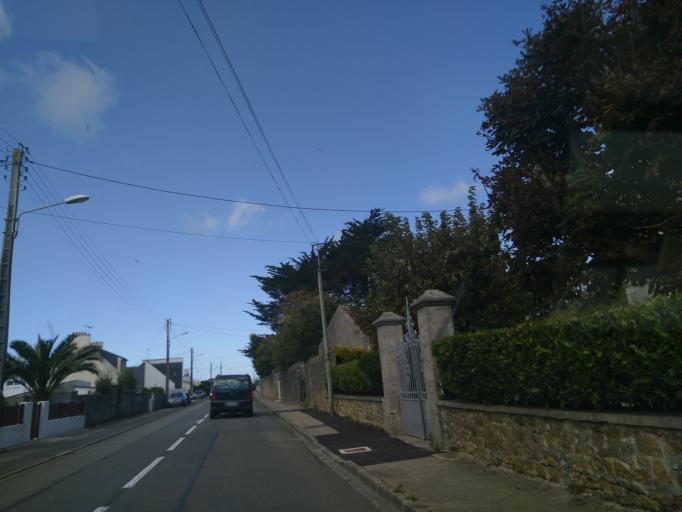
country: FR
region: Brittany
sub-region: Departement du Finistere
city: Crozon
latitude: 48.2465
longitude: -4.4967
